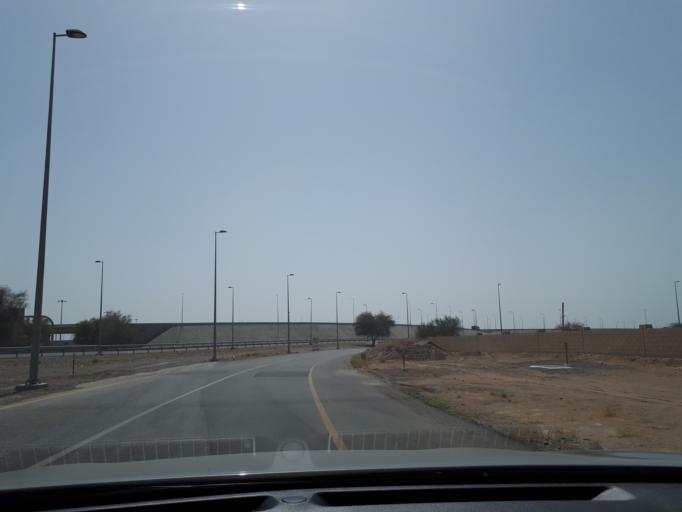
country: OM
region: Al Batinah
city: Barka'
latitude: 23.6879
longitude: 58.0293
